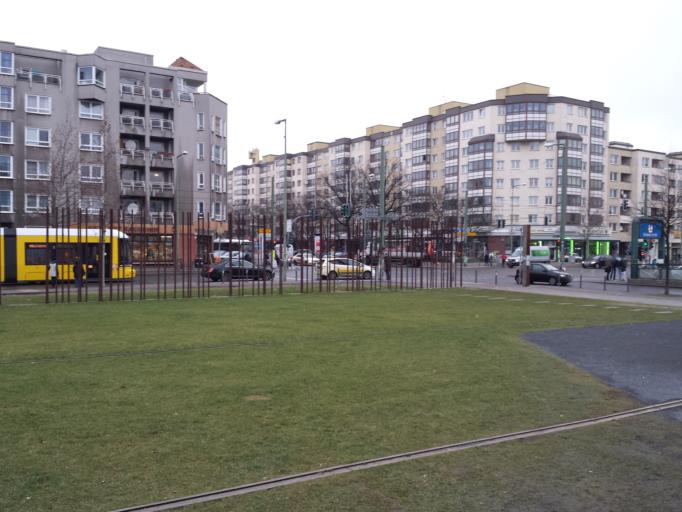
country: DE
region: Berlin
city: Gesundbrunnen
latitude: 52.5378
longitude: 13.3957
